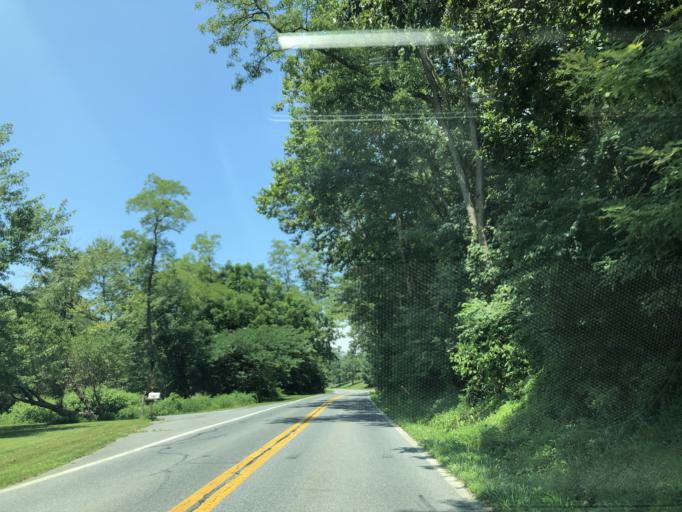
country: US
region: Maryland
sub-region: Carroll County
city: Westminster
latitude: 39.5256
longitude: -76.9532
